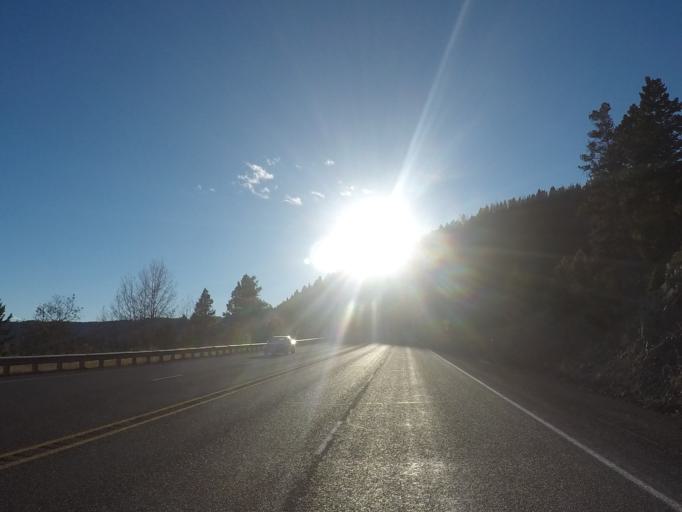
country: US
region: Montana
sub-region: Lewis and Clark County
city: Helena West Side
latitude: 46.5818
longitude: -112.2721
